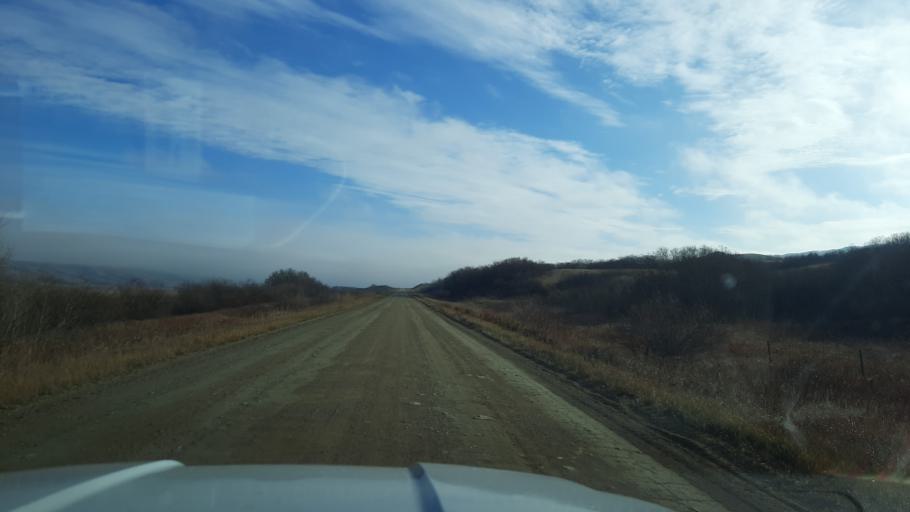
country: CA
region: Saskatchewan
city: Pilot Butte
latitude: 50.7838
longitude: -104.2396
